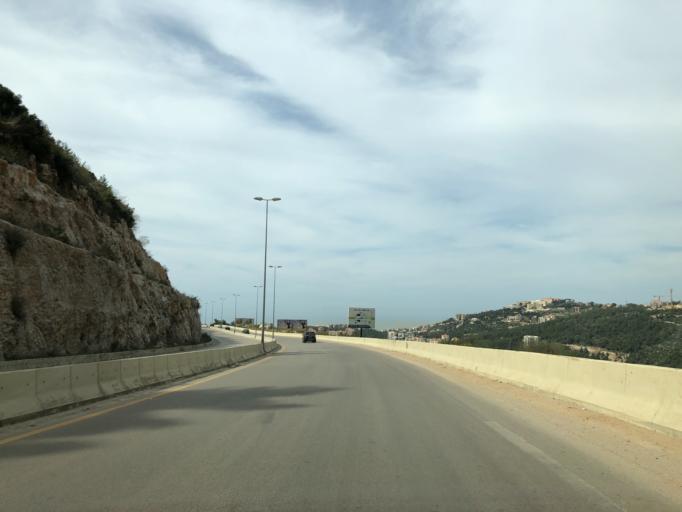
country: LB
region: Mont-Liban
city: Jdaidet el Matn
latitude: 33.8986
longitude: 35.6471
